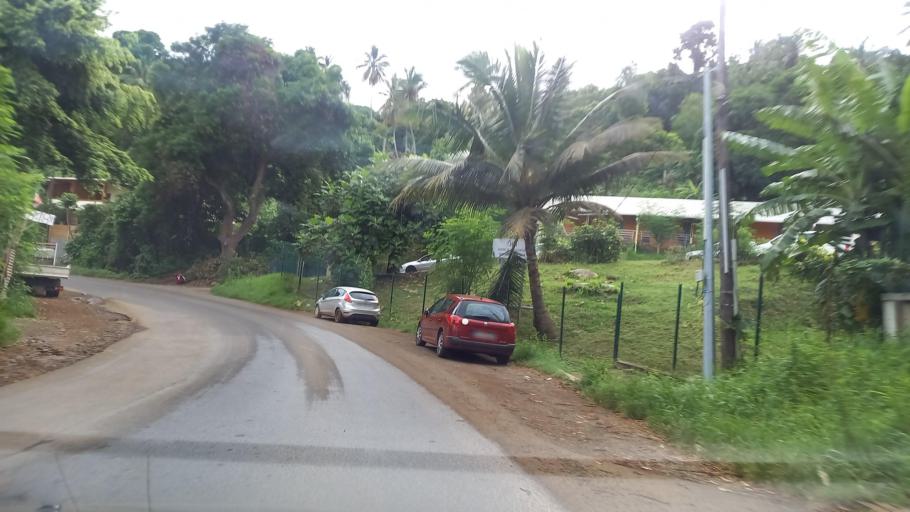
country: YT
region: Sada
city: Sada
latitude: -12.8556
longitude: 45.1029
